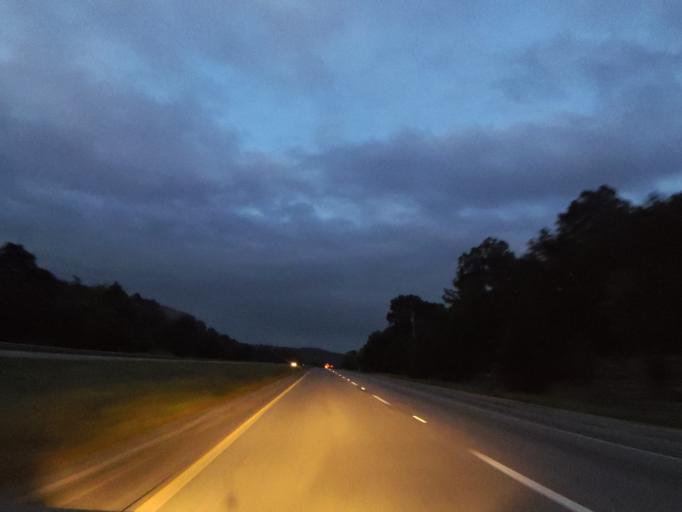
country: US
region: Alabama
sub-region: Jackson County
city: Scottsboro
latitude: 34.6206
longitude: -86.2050
